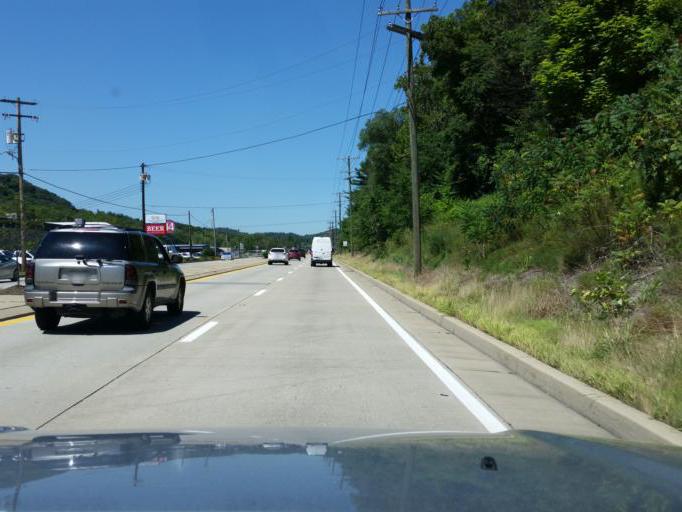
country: US
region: Pennsylvania
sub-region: Westmoreland County
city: Murrysville
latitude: 40.4261
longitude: -79.6758
